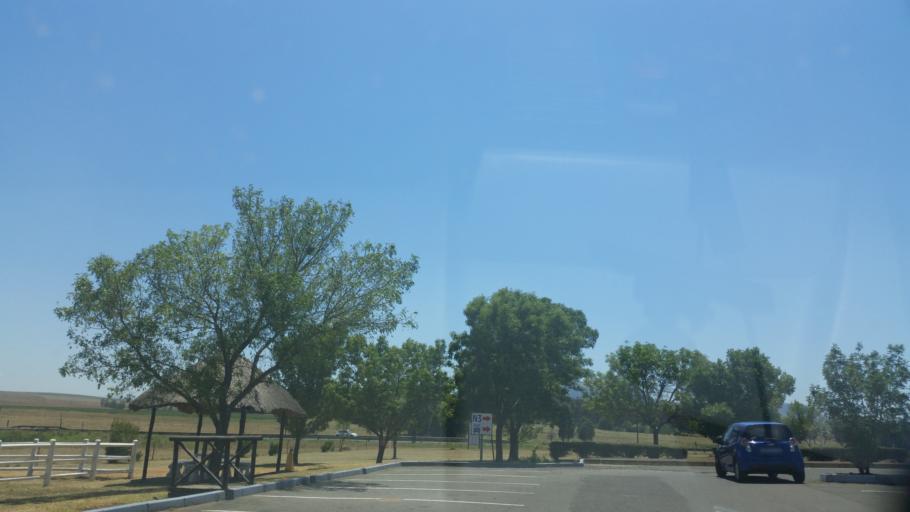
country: ZA
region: Orange Free State
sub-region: Thabo Mofutsanyana District Municipality
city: Harrismith
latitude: -28.1895
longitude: 29.0883
